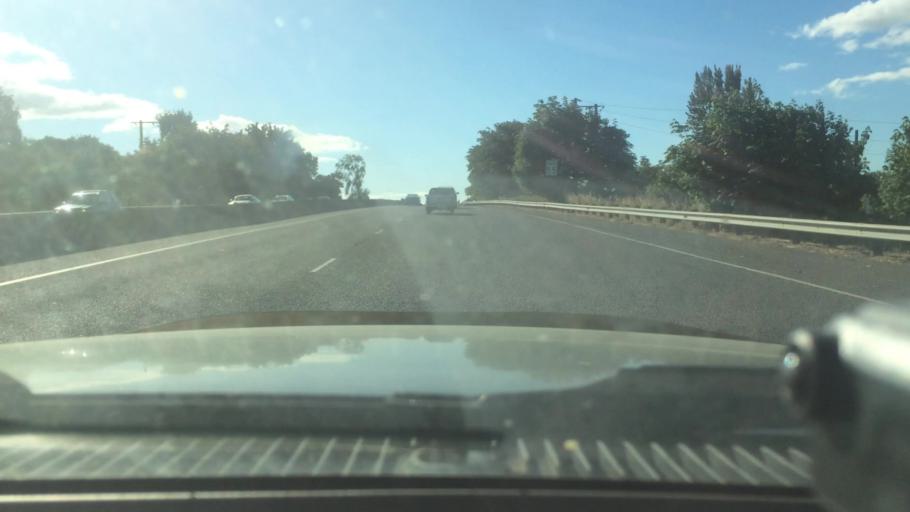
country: US
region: Oregon
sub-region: Lane County
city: Eugene
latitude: 44.0941
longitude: -123.1043
